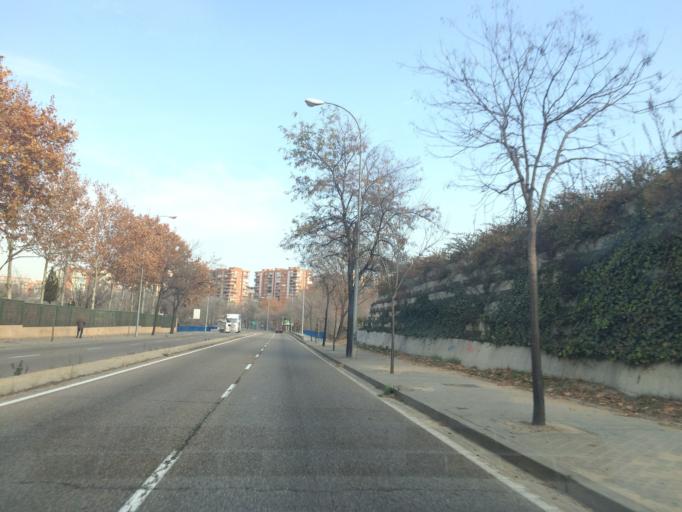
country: ES
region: Madrid
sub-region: Provincia de Madrid
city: Tetuan de las Victorias
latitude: 40.4674
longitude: -3.7139
